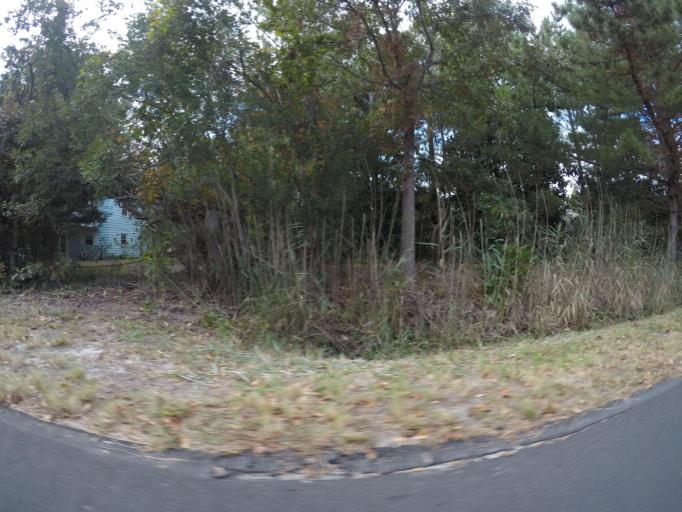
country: US
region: Delaware
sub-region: Sussex County
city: Rehoboth Beach
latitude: 38.7290
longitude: -75.0797
